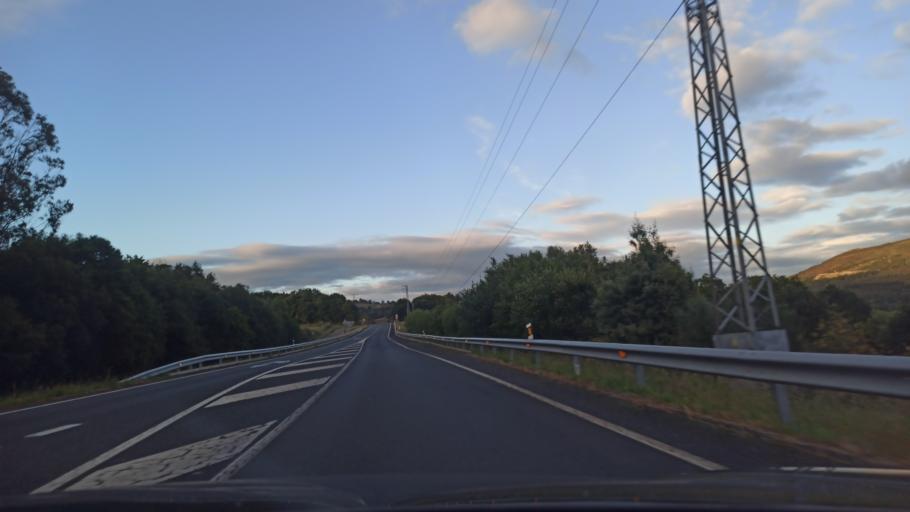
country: ES
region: Galicia
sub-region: Provincia de Pontevedra
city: Rodeiro
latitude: 42.7668
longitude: -7.9883
